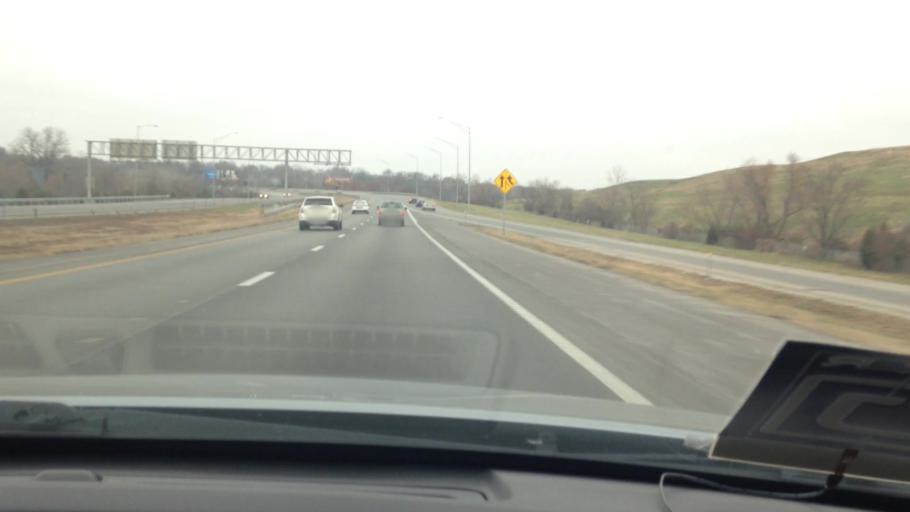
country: US
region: Kansas
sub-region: Johnson County
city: Leawood
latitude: 38.9754
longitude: -94.5458
